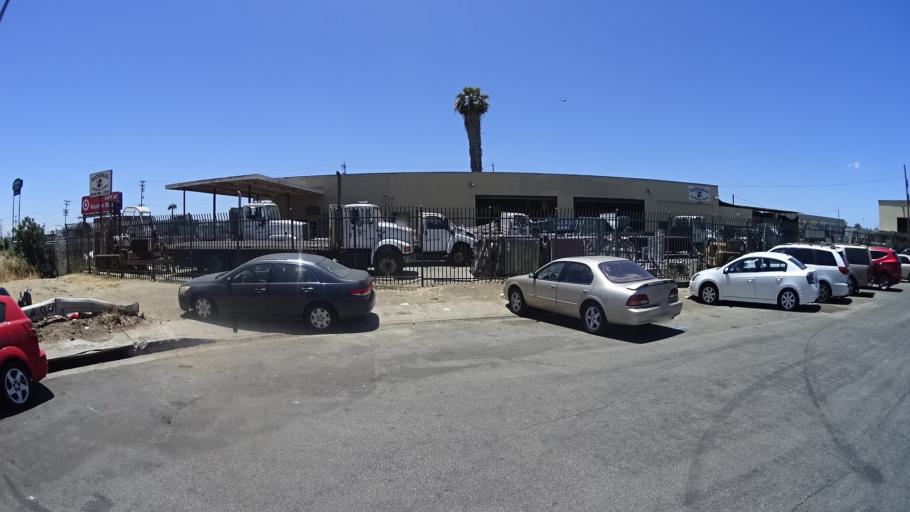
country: US
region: California
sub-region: Los Angeles County
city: Van Nuys
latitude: 34.2157
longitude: -118.4665
